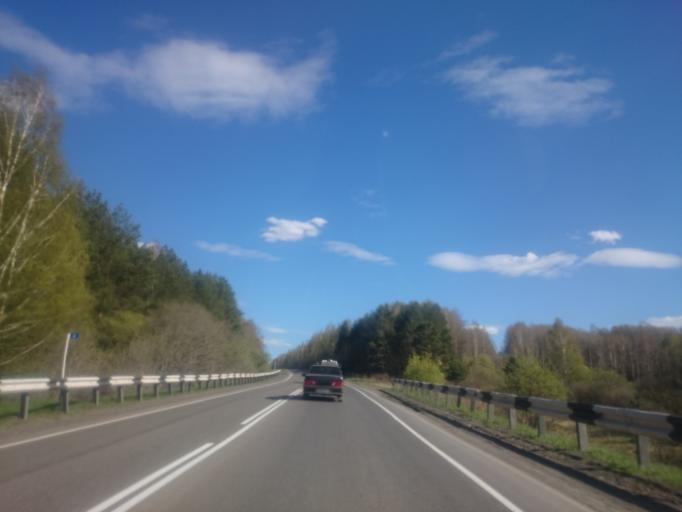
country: RU
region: Sverdlovsk
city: Lesnoy
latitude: 57.6231
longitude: 63.1644
